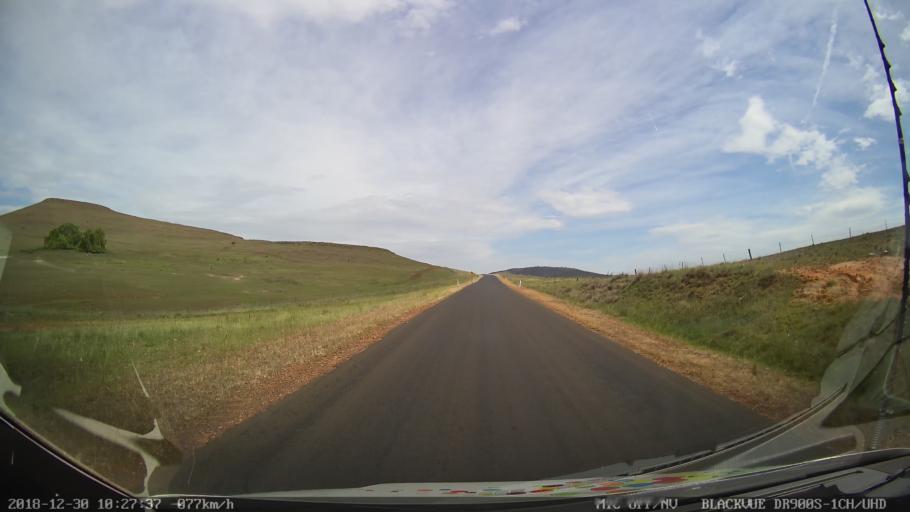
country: AU
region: New South Wales
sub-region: Snowy River
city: Berridale
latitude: -36.5121
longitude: 148.9306
